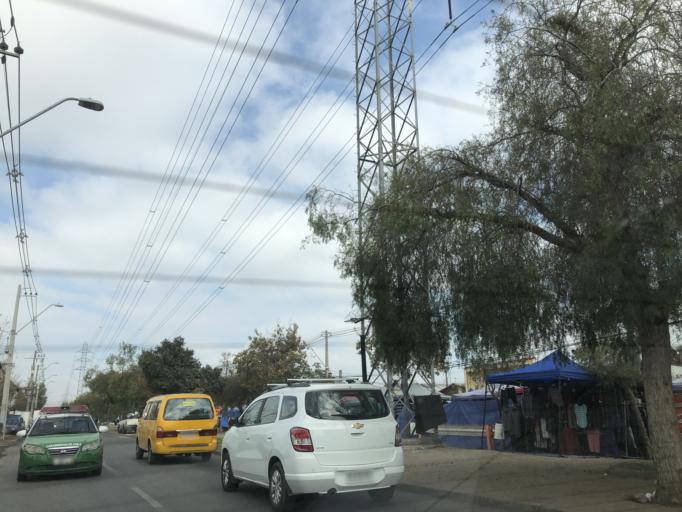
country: CL
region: Santiago Metropolitan
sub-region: Provincia de Cordillera
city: Puente Alto
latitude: -33.5839
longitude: -70.5972
